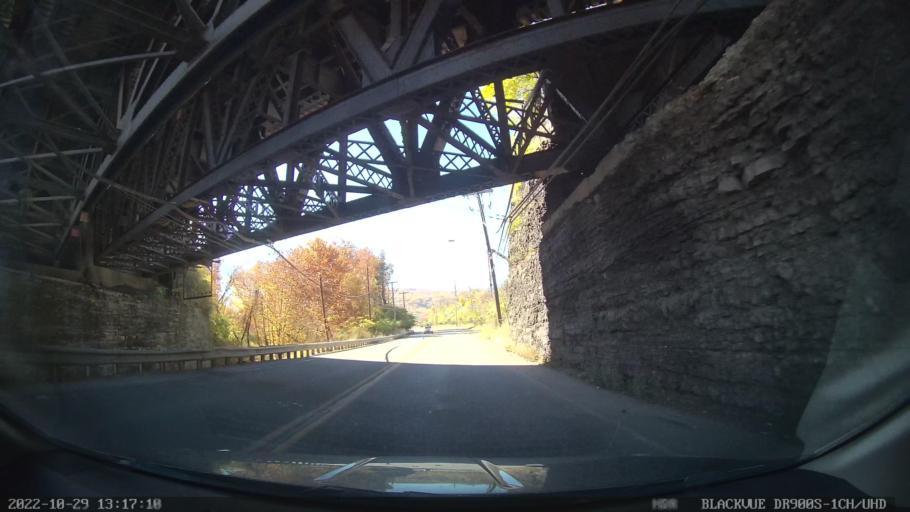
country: US
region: Pennsylvania
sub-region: Northampton County
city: Freemansburg
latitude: 40.6119
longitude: -75.3364
